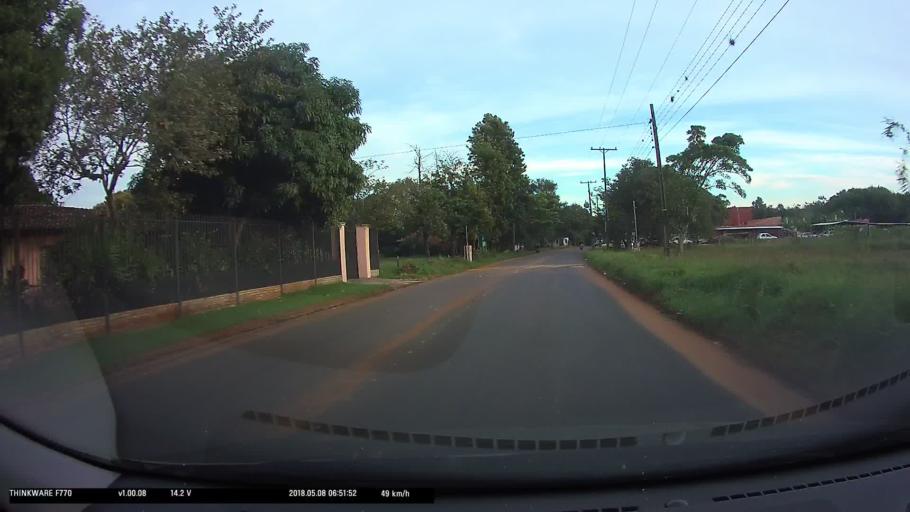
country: PY
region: Central
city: Limpio
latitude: -25.2392
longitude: -57.4635
